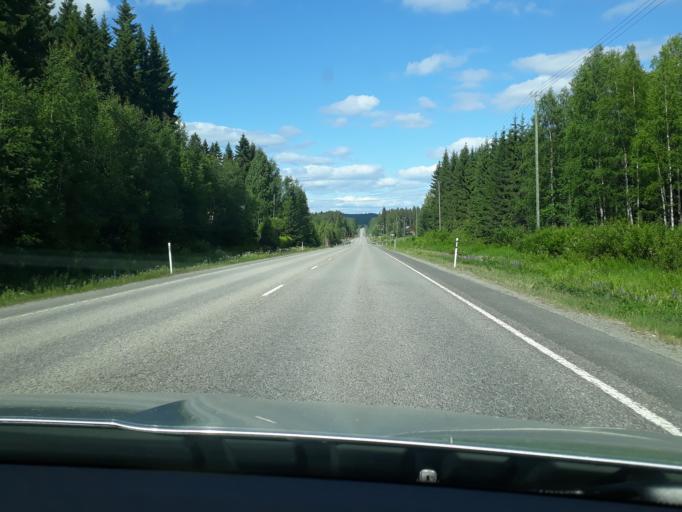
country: FI
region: Central Finland
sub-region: AEaenekoski
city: AEaenekoski
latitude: 62.6516
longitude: 25.7183
